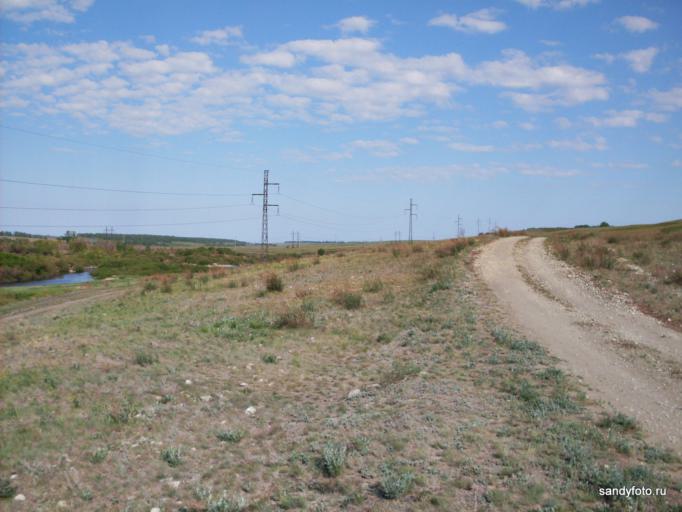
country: RU
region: Chelyabinsk
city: Troitsk
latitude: 54.1244
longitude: 61.4768
